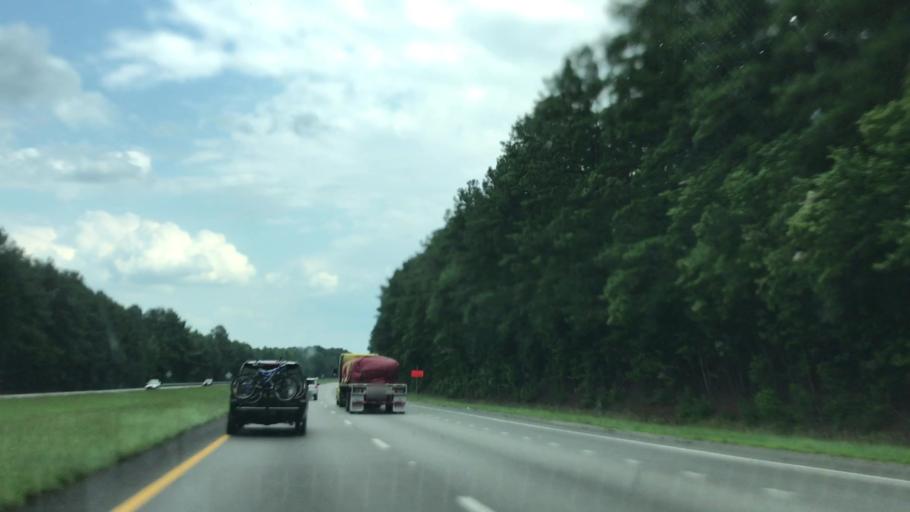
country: US
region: South Carolina
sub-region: Richland County
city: Blythewood
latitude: 34.3021
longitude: -80.9980
